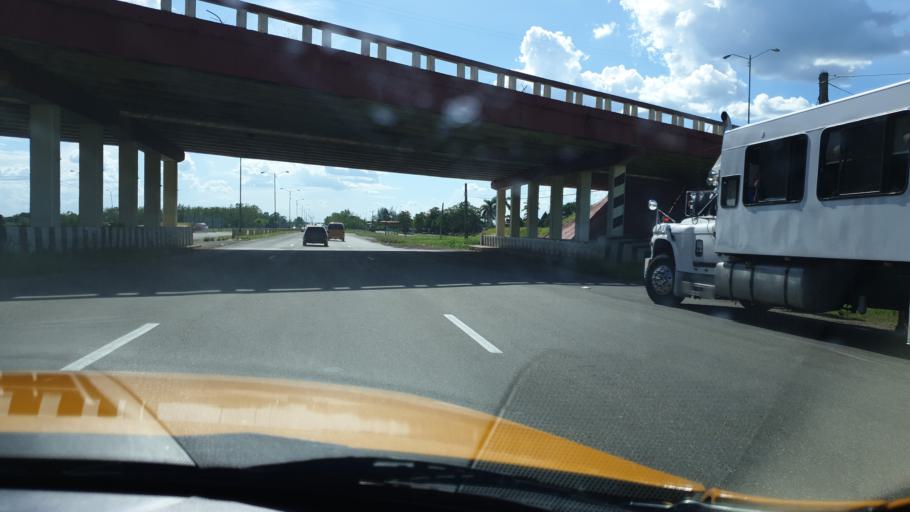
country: CU
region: Cienfuegos
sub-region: Municipio de Aguada de Pasajeros
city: Aguada de Pasajeros
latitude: 22.4037
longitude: -80.8627
